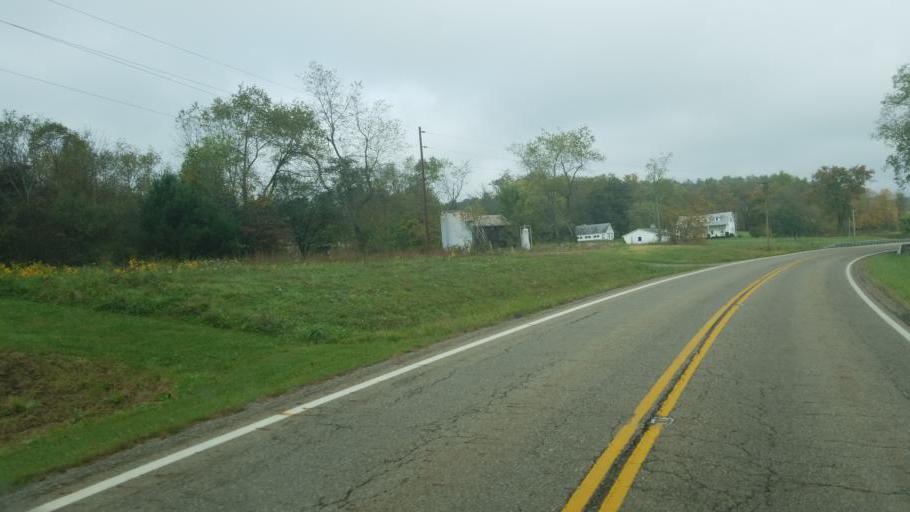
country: US
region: Ohio
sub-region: Tuscarawas County
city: Rockford
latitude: 40.5660
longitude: -81.2572
